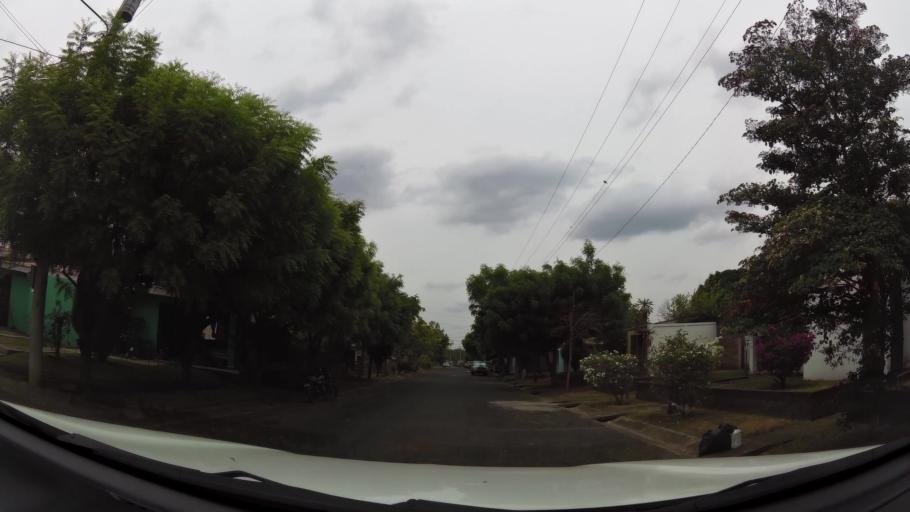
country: NI
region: Masaya
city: Ticuantepe
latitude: 12.0752
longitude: -86.1758
